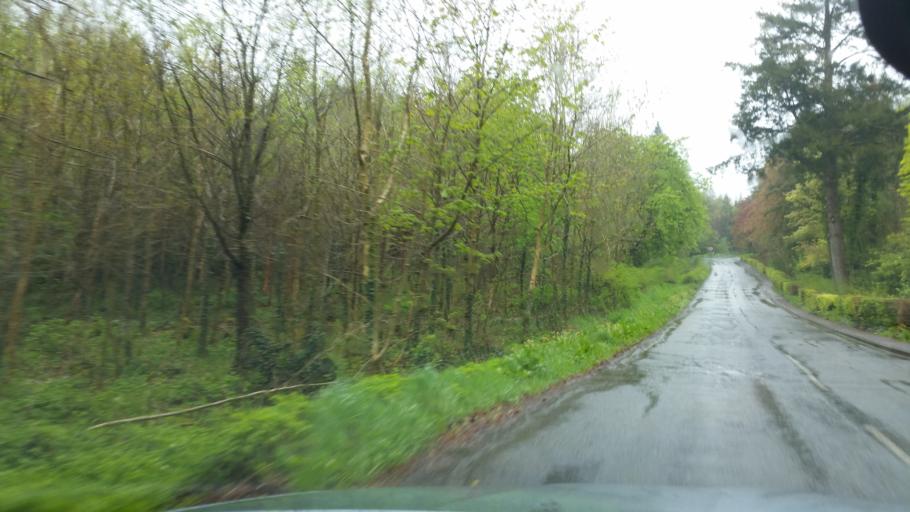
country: GB
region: Northern Ireland
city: Fivemiletown
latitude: 54.3812
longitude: -7.3140
